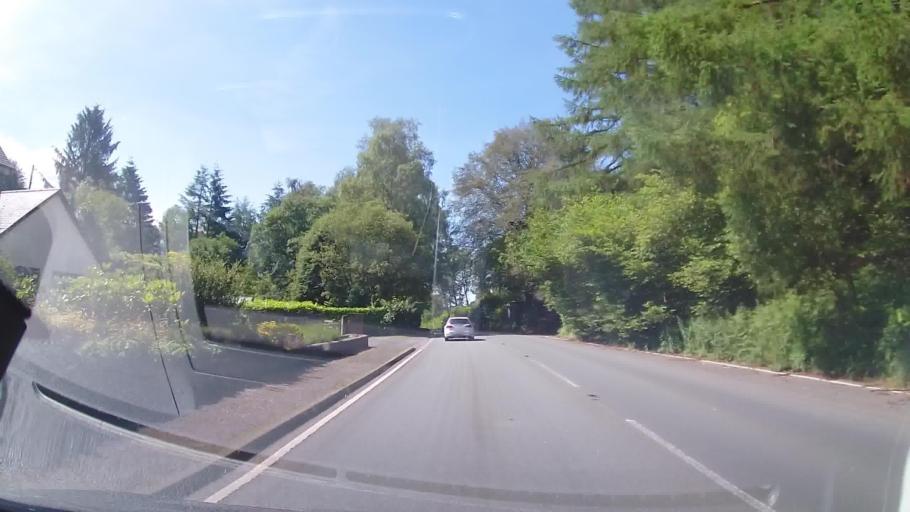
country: GB
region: Wales
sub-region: Sir Powys
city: Machynlleth
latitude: 52.5732
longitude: -3.9518
